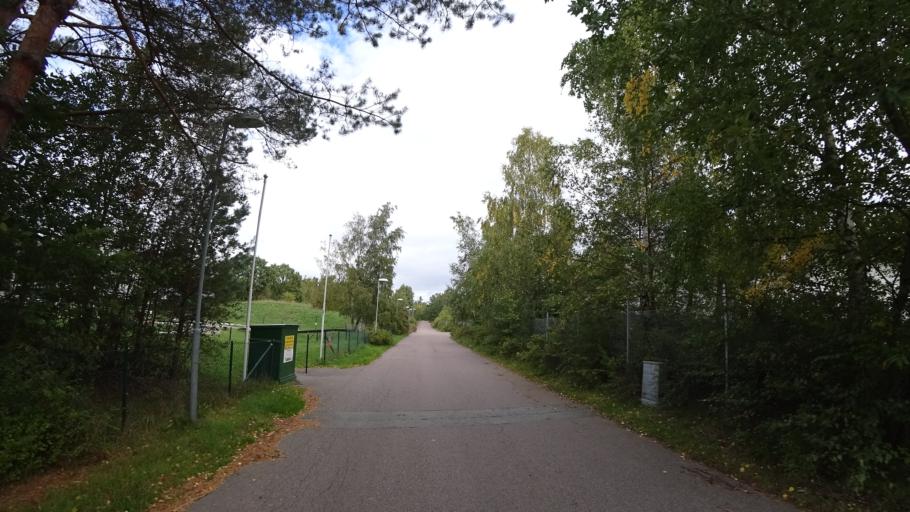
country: SE
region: Skane
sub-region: Kavlinge Kommun
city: Kaevlinge
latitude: 55.7715
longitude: 13.0771
